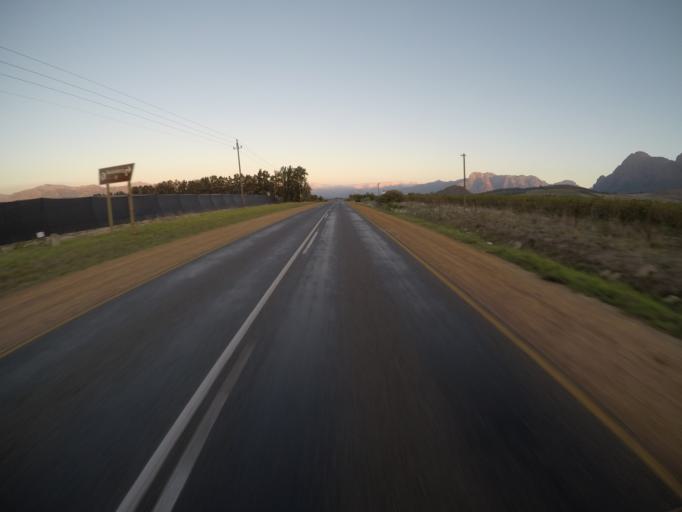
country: ZA
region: Western Cape
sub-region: Cape Winelands District Municipality
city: Paarl
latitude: -33.8182
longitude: 18.9220
